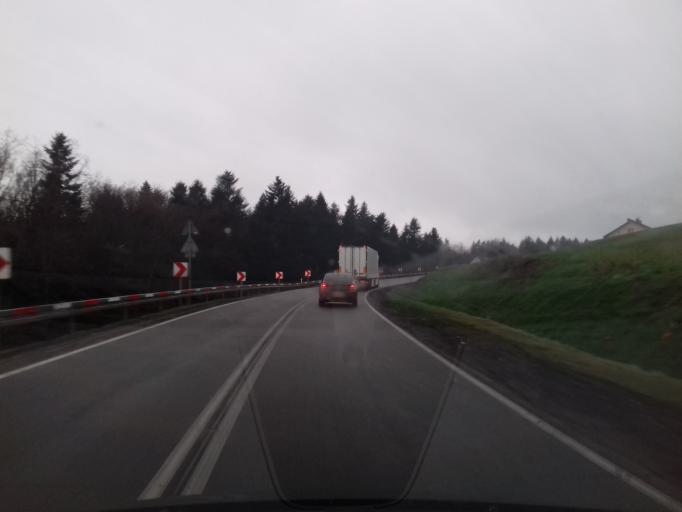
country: PL
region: Lesser Poland Voivodeship
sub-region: Powiat nowosadecki
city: Podegrodzie
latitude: 49.6499
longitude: 20.5844
